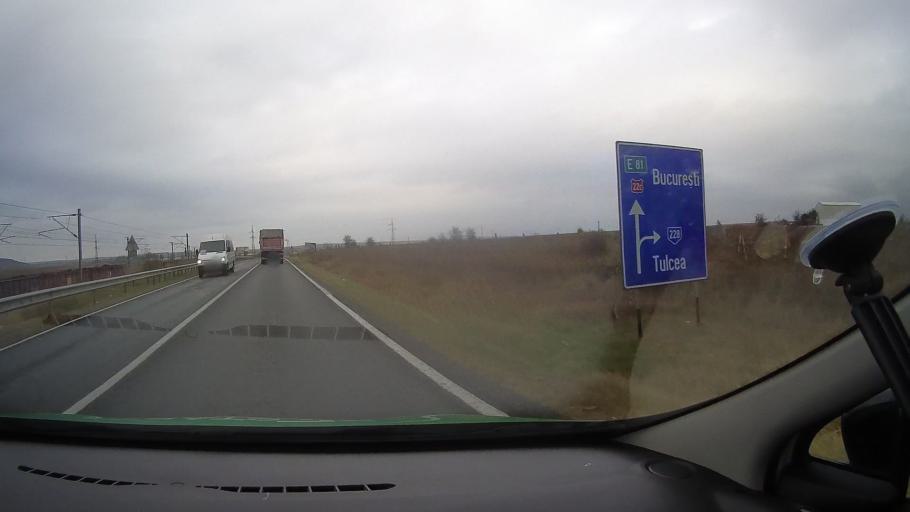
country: RO
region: Constanta
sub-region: Comuna Poarta Alba
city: Poarta Alba
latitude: 44.2309
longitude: 28.3779
